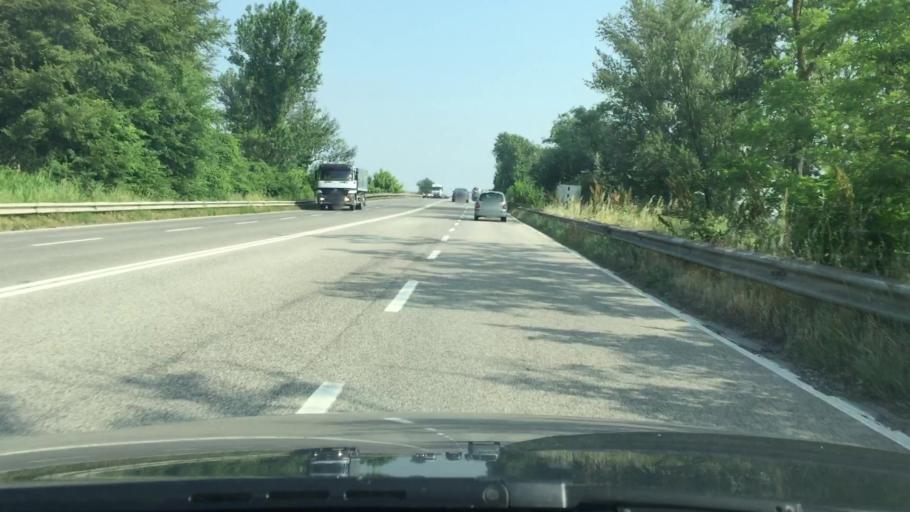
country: IT
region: Emilia-Romagna
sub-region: Provincia di Ferrara
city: Gaibanella-Sant'Edigio
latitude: 44.7994
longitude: 11.6368
